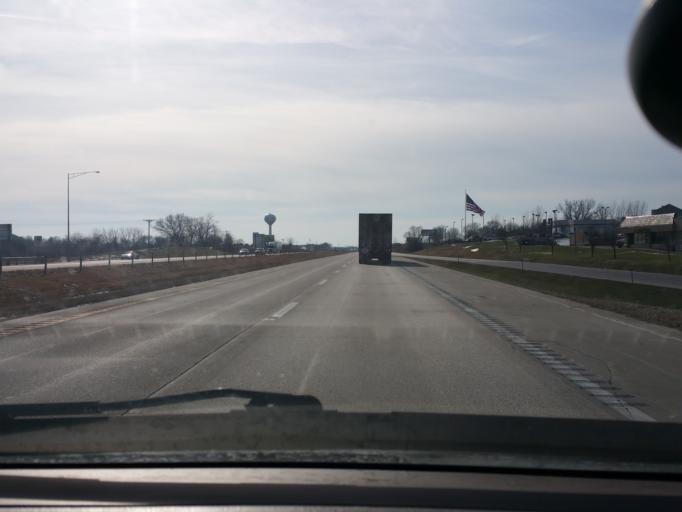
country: US
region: Missouri
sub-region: Clay County
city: Kearney
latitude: 39.3675
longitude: -94.3728
